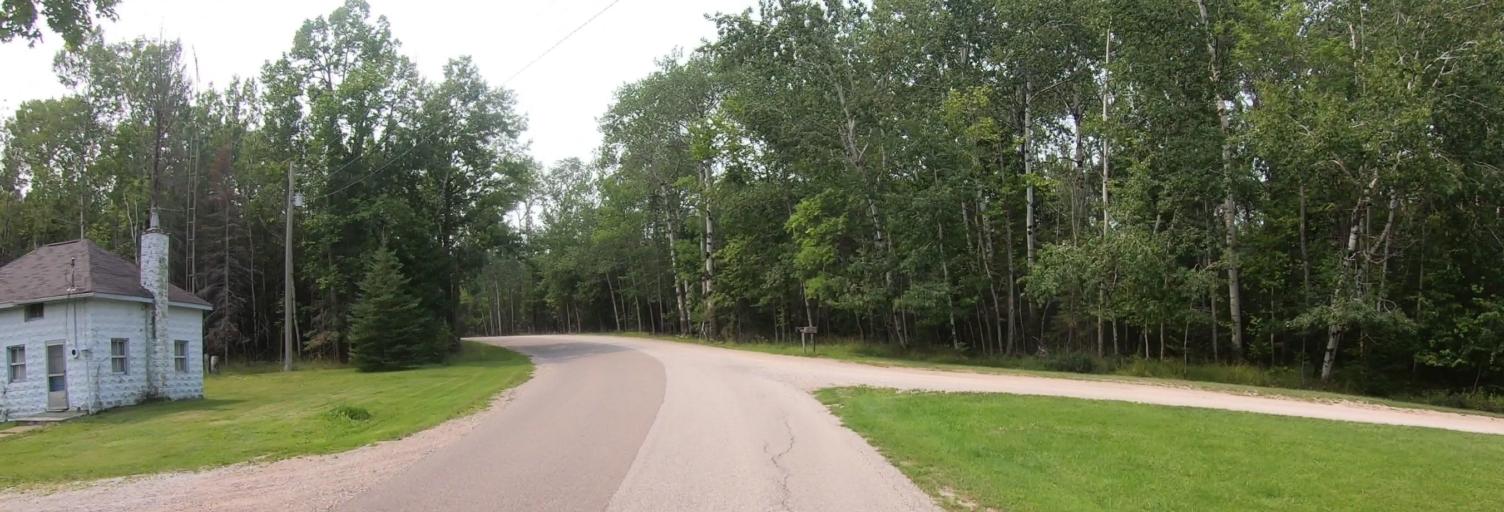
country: CA
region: Ontario
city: Thessalon
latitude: 46.0311
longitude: -83.6749
